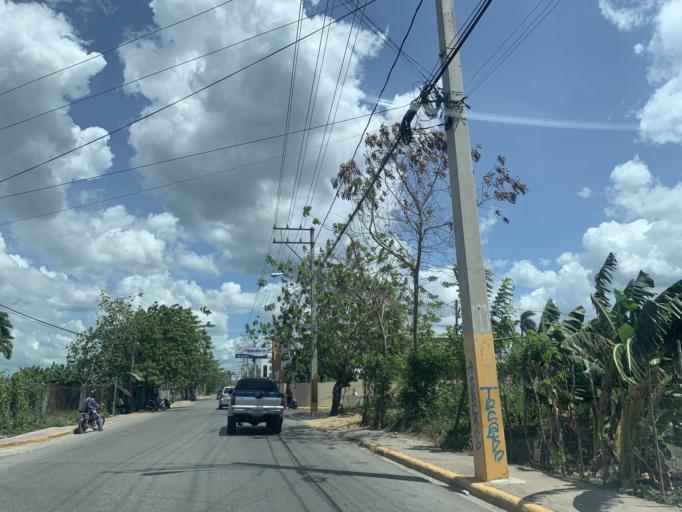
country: DO
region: Espaillat
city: Jamao al Norte
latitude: 19.6645
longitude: -70.3660
